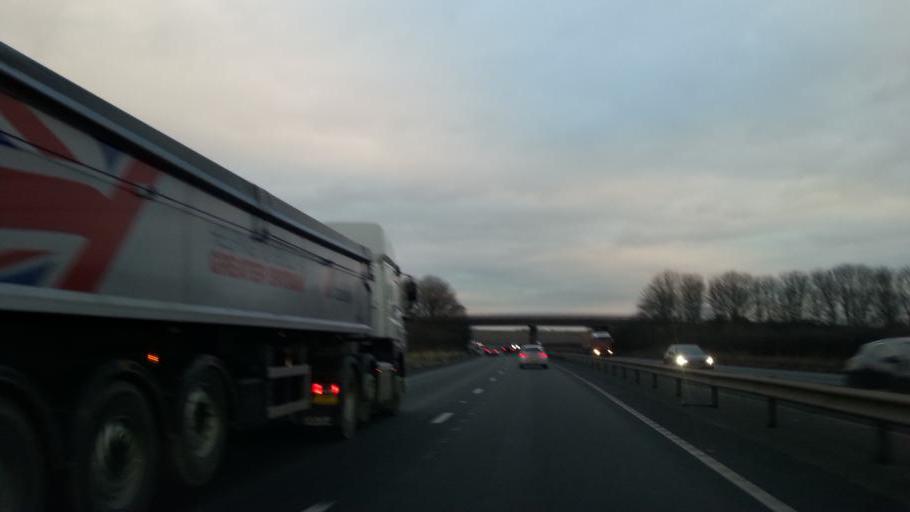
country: GB
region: England
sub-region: Nottinghamshire
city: Newark on Trent
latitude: 53.0627
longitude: -0.7652
